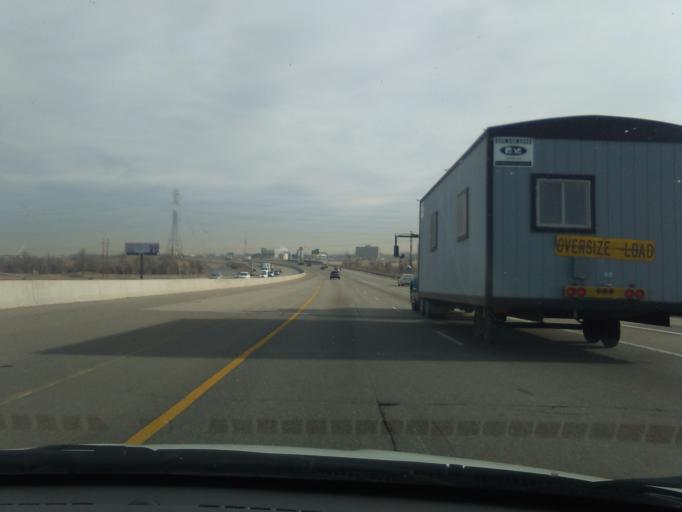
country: US
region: Colorado
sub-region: Adams County
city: Welby
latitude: 39.8251
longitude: -104.9539
